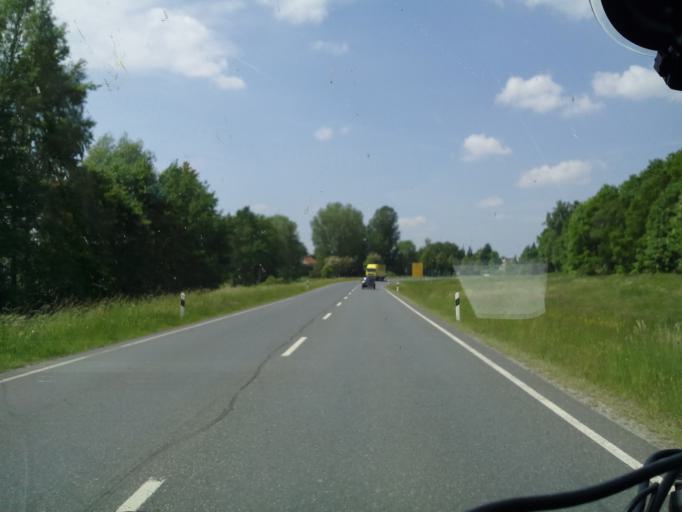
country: DE
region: Bavaria
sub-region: Upper Franconia
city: Mainleus
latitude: 50.1013
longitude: 11.3982
